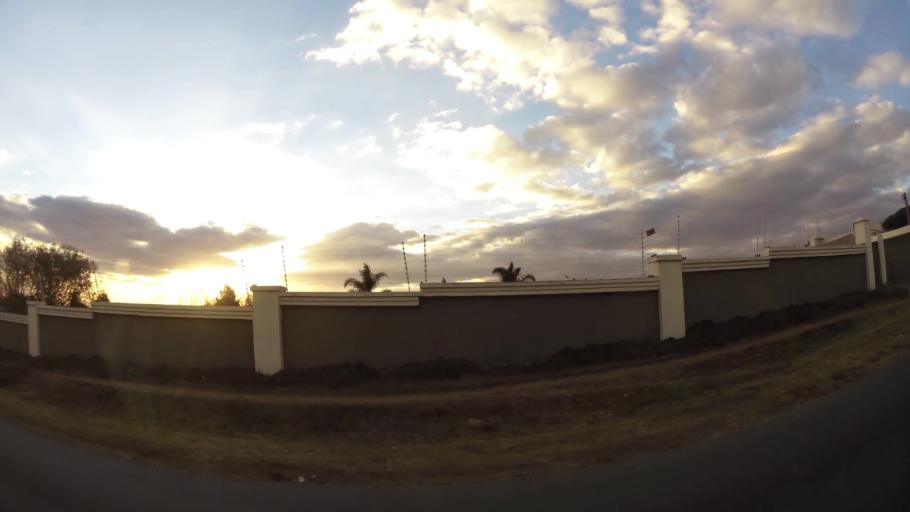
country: ZA
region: Gauteng
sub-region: City of Johannesburg Metropolitan Municipality
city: Midrand
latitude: -26.0145
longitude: 28.1588
